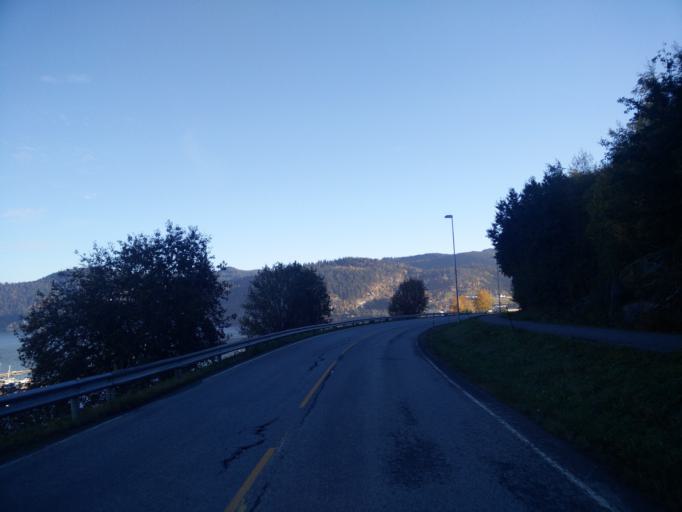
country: NO
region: Sor-Trondelag
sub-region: Skaun
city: Borsa
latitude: 63.3324
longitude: 10.0688
